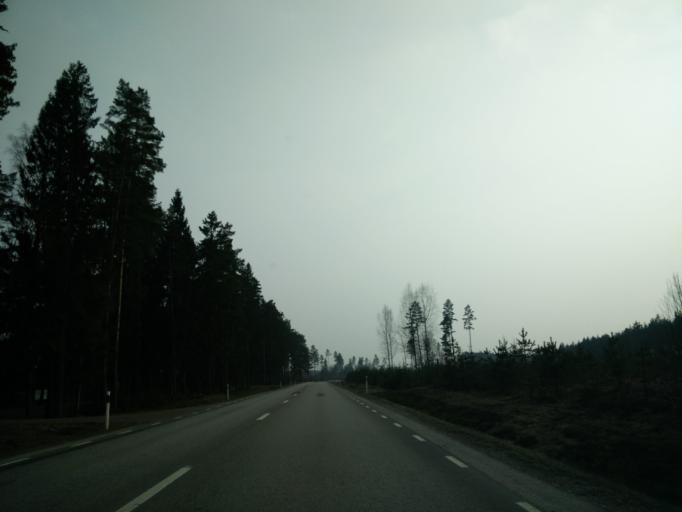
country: SE
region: Vaermland
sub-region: Forshaga Kommun
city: Forshaga
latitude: 59.5023
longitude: 13.4344
